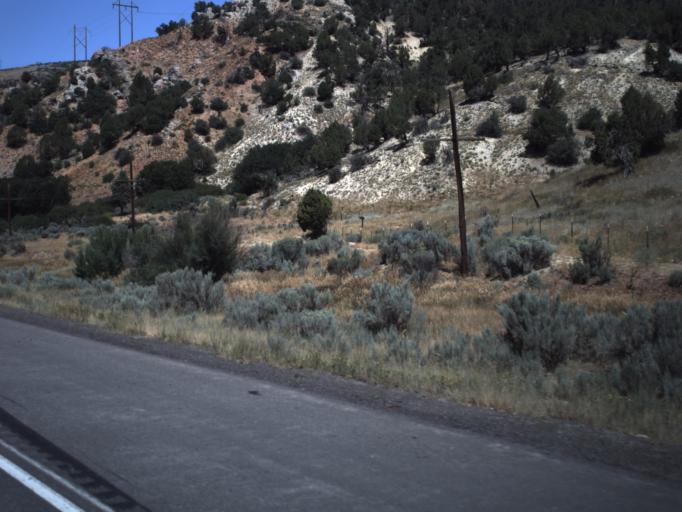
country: US
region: Utah
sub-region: Utah County
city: Mapleton
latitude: 39.9855
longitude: -111.3626
